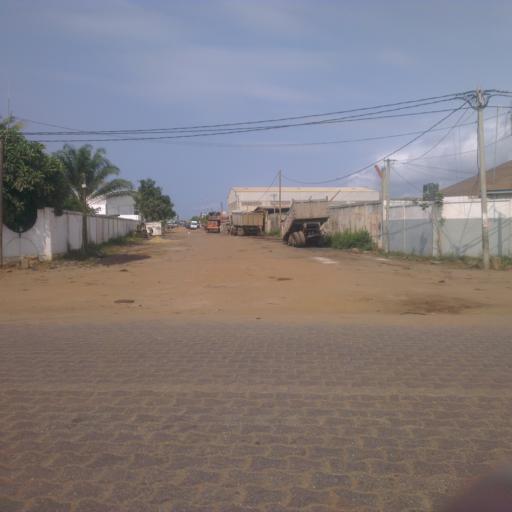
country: TG
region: Maritime
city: Lome
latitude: 6.1479
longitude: 1.2733
